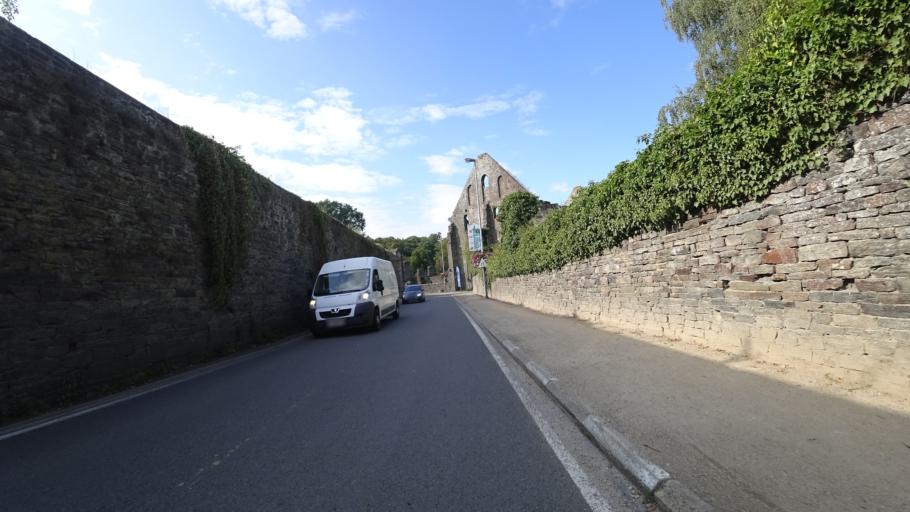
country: BE
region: Wallonia
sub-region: Province du Brabant Wallon
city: Villers-la-Ville
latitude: 50.5897
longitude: 4.5296
